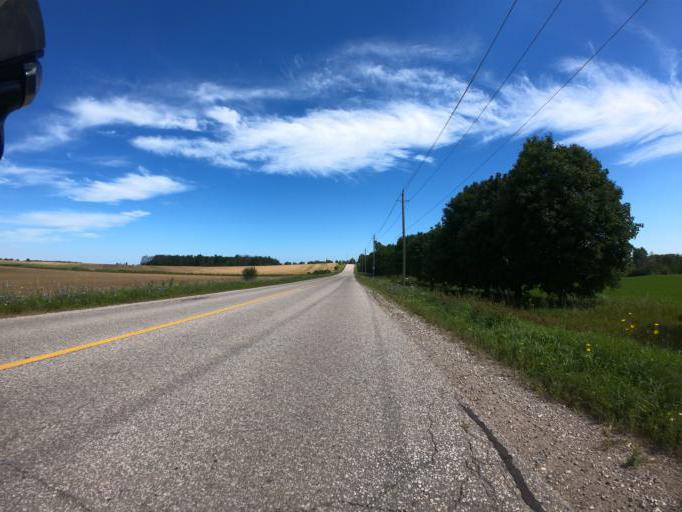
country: CA
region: Ontario
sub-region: Wellington County
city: Guelph
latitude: 43.5407
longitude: -80.3832
